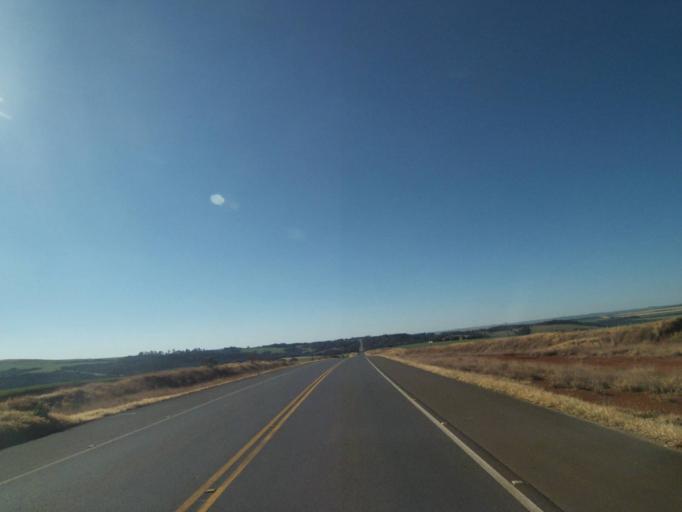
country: BR
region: Parana
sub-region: Tibagi
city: Tibagi
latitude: -24.6240
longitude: -50.4521
